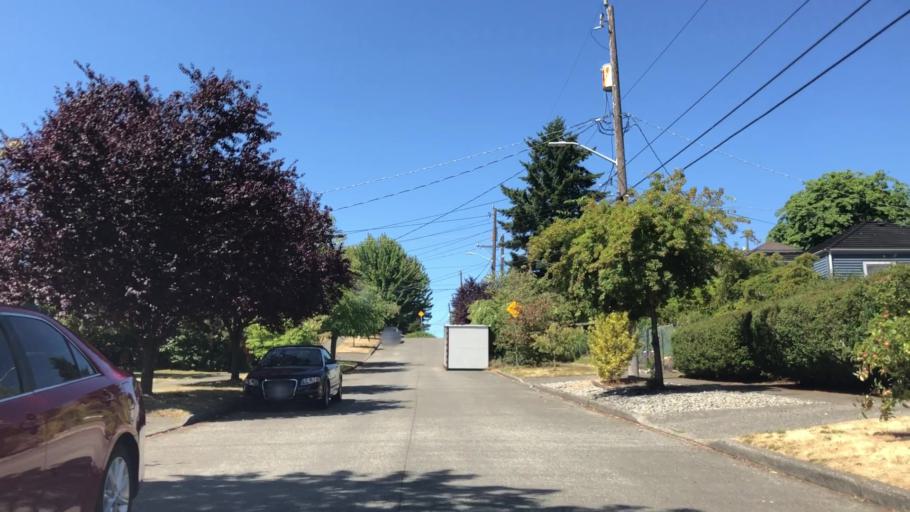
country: US
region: Washington
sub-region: King County
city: Shoreline
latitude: 47.6920
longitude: -122.3459
